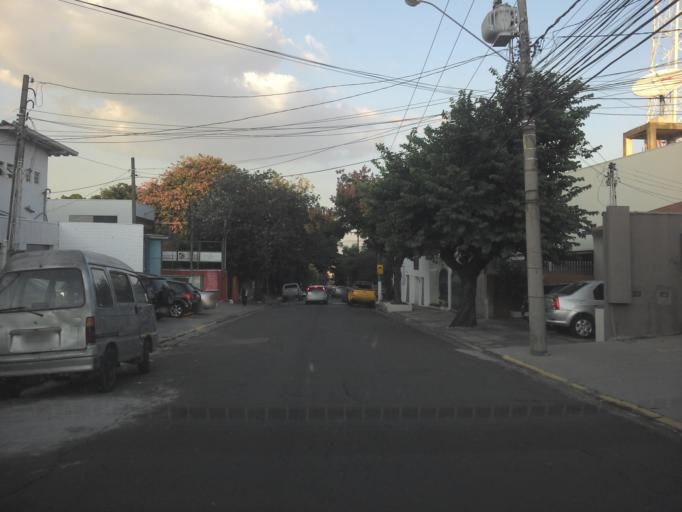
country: BR
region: Sao Paulo
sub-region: Campinas
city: Campinas
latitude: -22.8897
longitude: -47.0745
